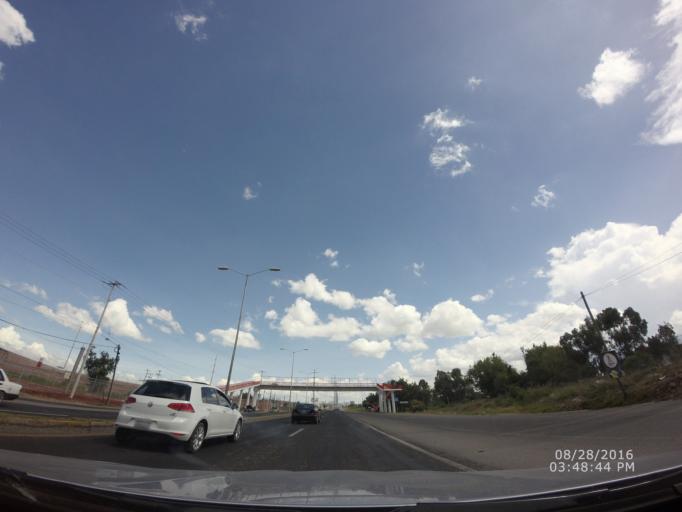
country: MX
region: Hidalgo
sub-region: Mineral de la Reforma
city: Los Tuzos
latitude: 20.0525
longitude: -98.7400
